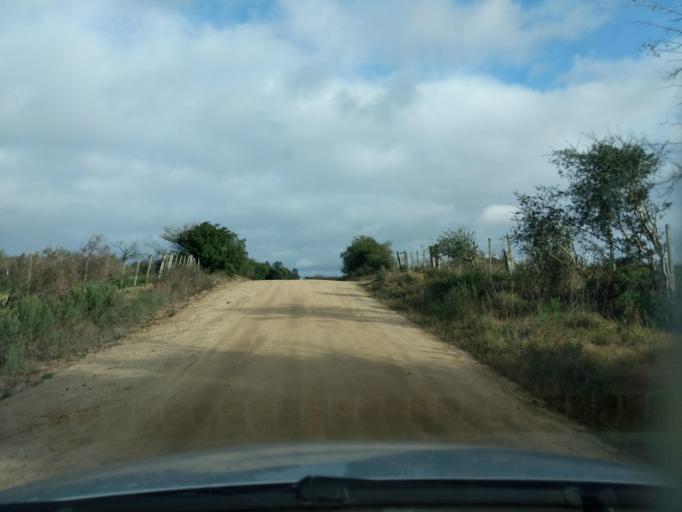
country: UY
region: Florida
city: Florida
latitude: -34.0596
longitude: -56.2127
